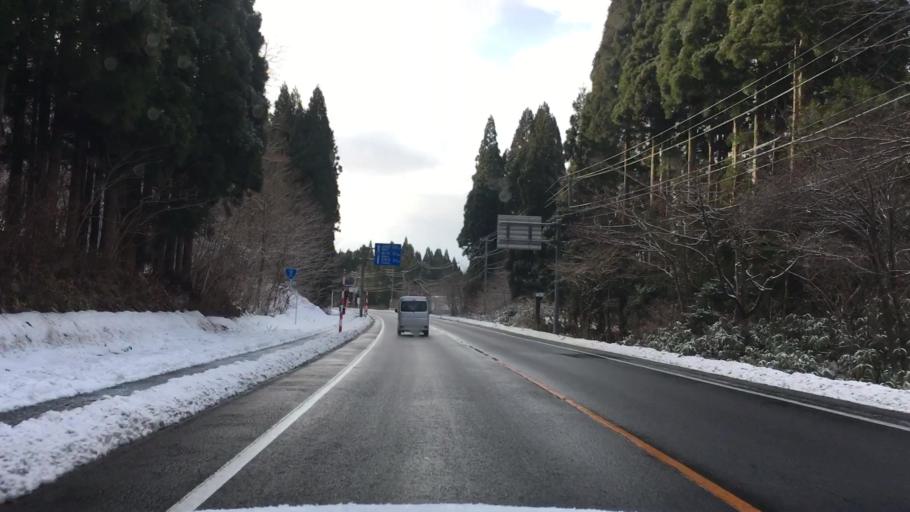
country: JP
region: Akita
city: Odate
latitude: 40.3849
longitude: 140.6037
